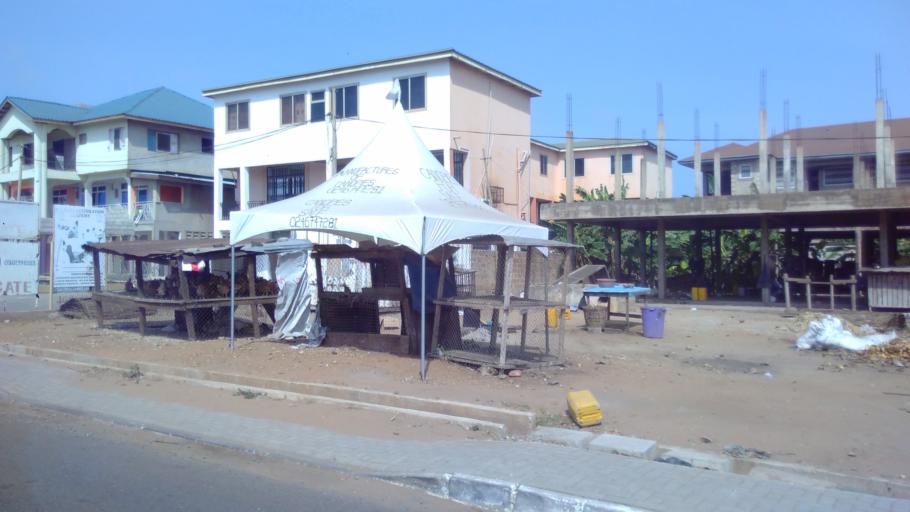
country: GH
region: Greater Accra
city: Nungua
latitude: 5.6159
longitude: -0.0729
